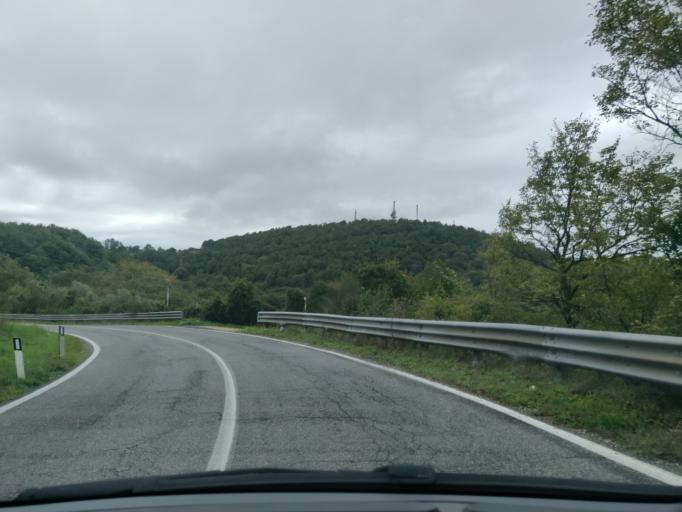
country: IT
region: Latium
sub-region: Citta metropolitana di Roma Capitale
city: Allumiere
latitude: 42.1477
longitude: 11.8958
